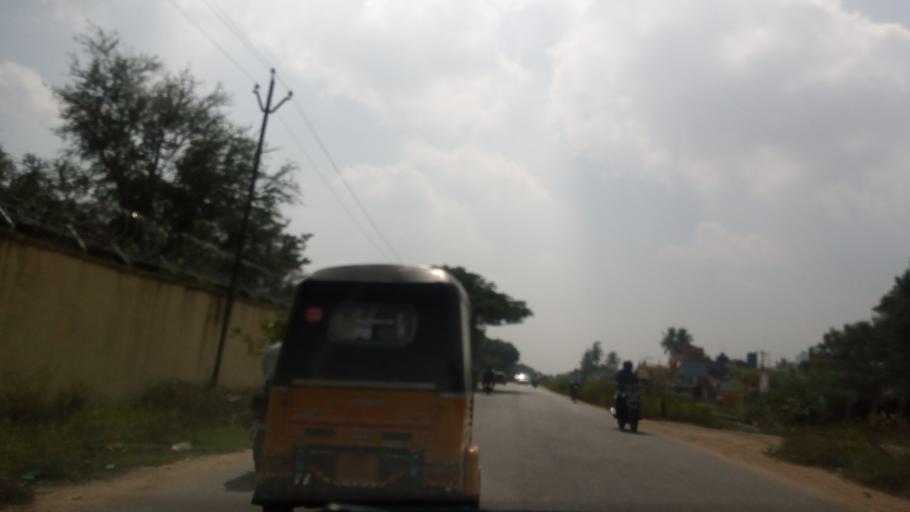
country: IN
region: Tamil Nadu
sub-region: Vellore
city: Arakkonam
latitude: 13.0689
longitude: 79.6728
